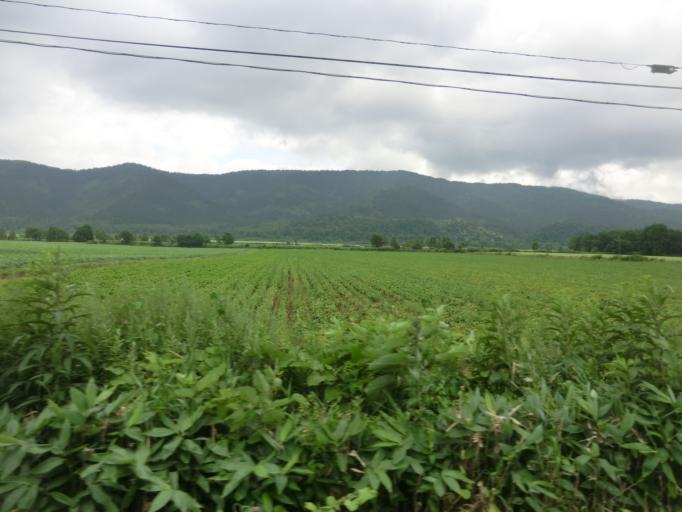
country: JP
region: Hokkaido
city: Nayoro
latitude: 44.1479
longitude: 142.1492
